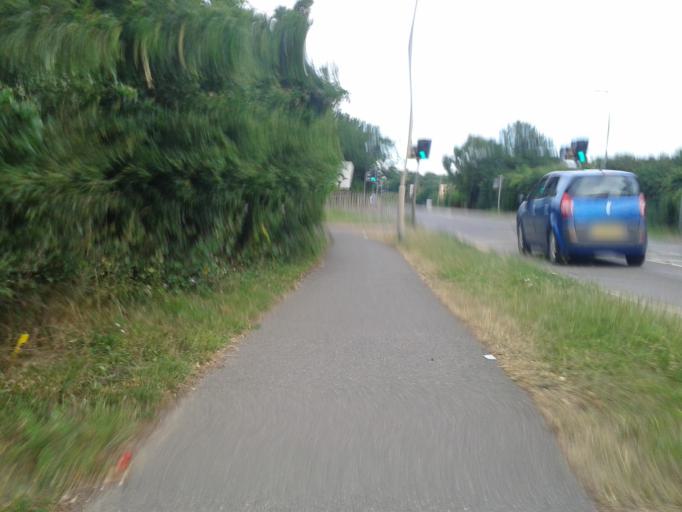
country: GB
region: England
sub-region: Cambridgeshire
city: Sawston
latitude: 52.1676
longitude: 0.1572
